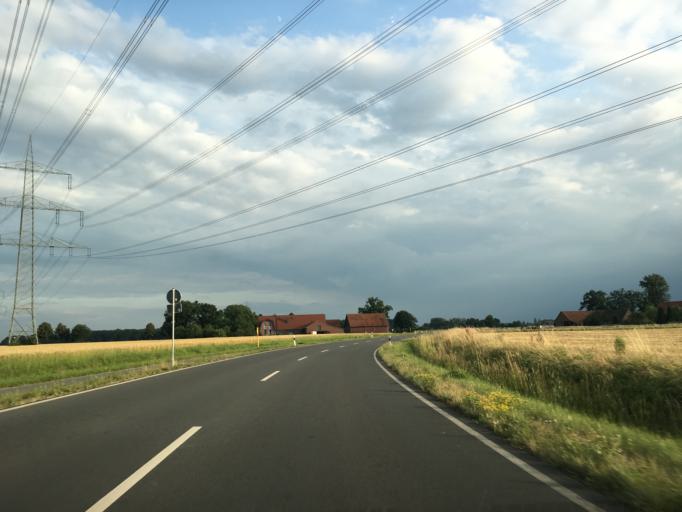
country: DE
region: North Rhine-Westphalia
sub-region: Regierungsbezirk Munster
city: Senden
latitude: 51.9415
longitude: 7.5275
